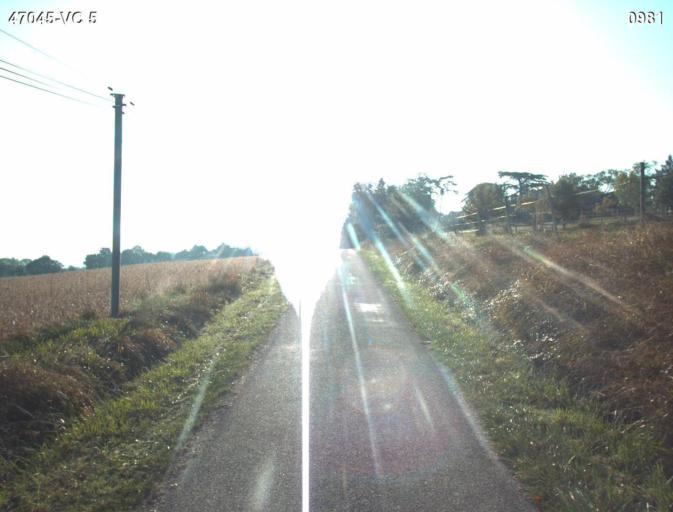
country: FR
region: Aquitaine
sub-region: Departement du Lot-et-Garonne
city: Nerac
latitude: 44.1386
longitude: 0.4054
